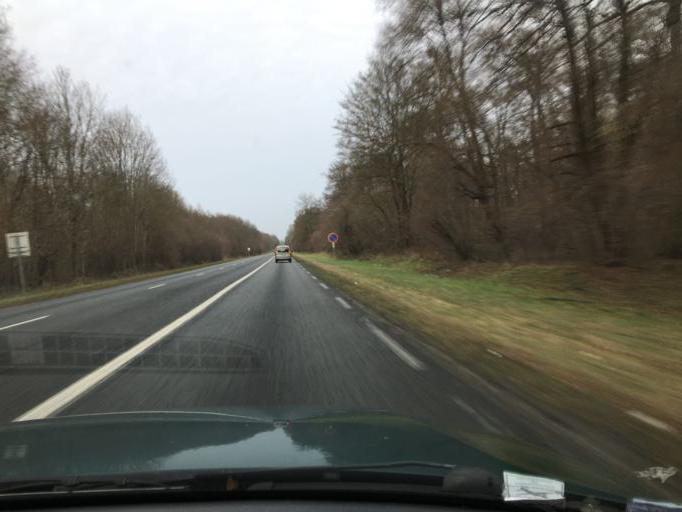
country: FR
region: Picardie
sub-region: Departement de l'Oise
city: Thiers-sur-Theve
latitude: 49.1748
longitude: 2.5627
